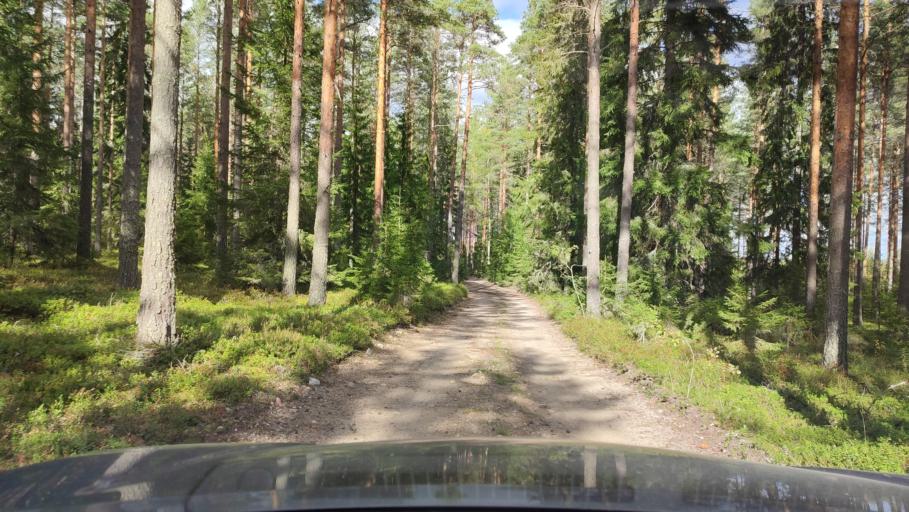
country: FI
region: Southern Ostrobothnia
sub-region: Suupohja
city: Karijoki
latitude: 62.2171
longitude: 21.6261
